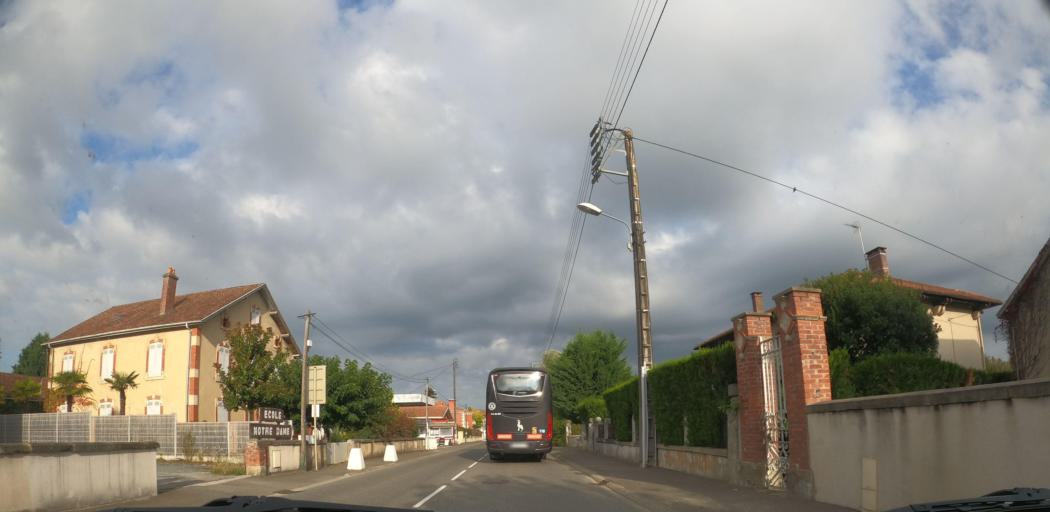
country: FR
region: Aquitaine
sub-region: Departement des Landes
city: Soustons
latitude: 43.7525
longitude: -1.3243
